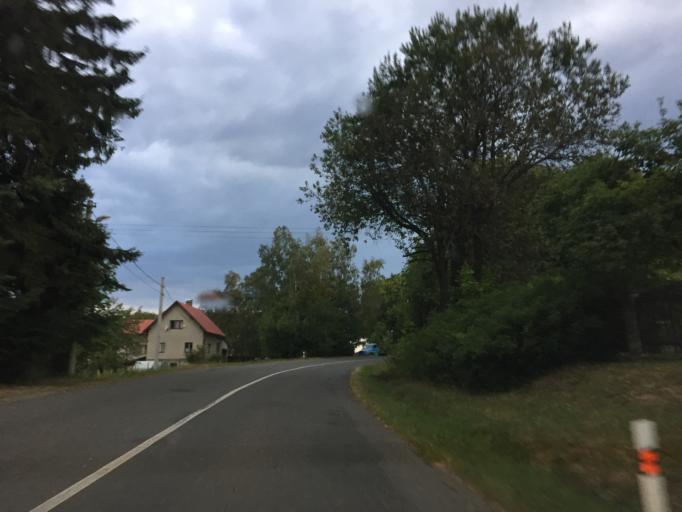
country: CZ
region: Liberecky
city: Mala Skala
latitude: 50.6848
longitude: 15.1832
